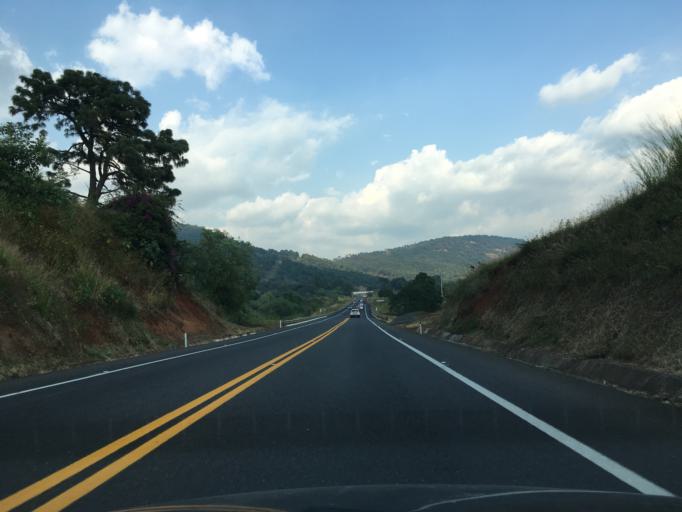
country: MX
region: Michoacan
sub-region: Ziracuaretiro
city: Patuan
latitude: 19.4264
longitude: -101.9194
